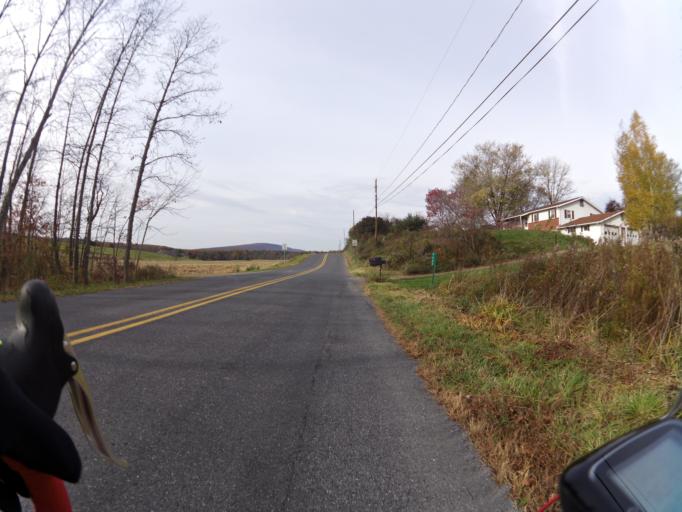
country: US
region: Pennsylvania
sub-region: Union County
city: New Columbia
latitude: 41.0498
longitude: -76.9368
